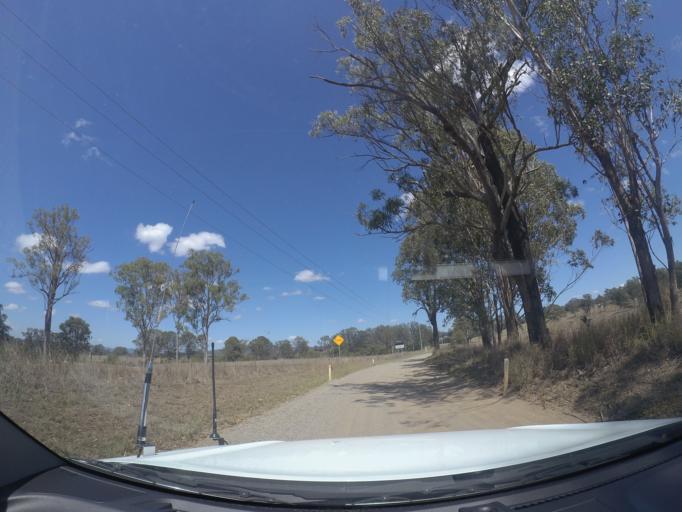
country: AU
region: Queensland
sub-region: Logan
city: Cedar Vale
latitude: -27.8388
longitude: 152.9214
